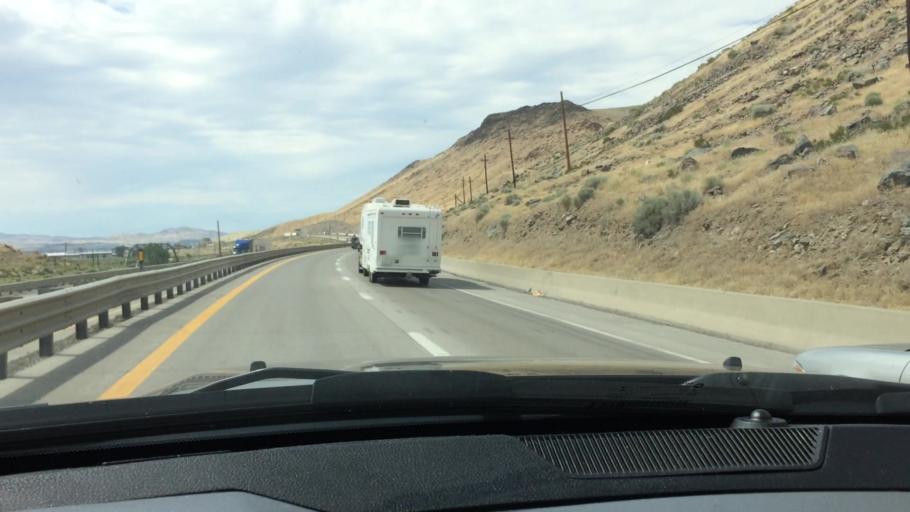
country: US
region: Nevada
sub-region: Washoe County
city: Sparks
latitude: 39.5165
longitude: -119.6819
